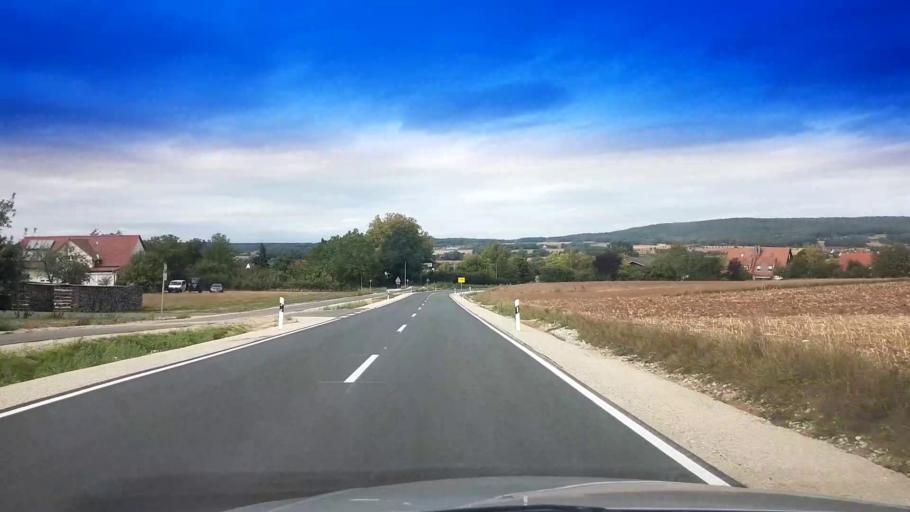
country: DE
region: Bavaria
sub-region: Upper Franconia
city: Frensdorf
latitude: 49.8109
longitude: 10.8709
